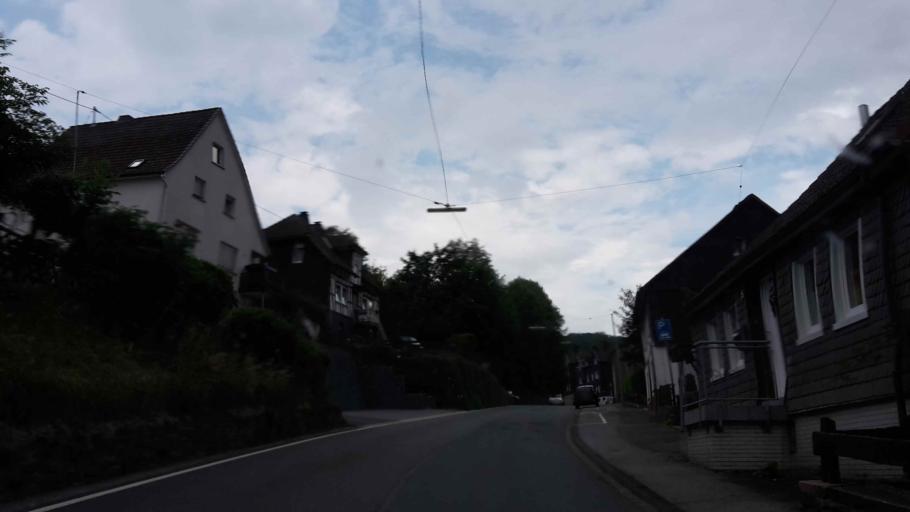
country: DE
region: North Rhine-Westphalia
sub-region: Regierungsbezirk Arnsberg
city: Lennestadt
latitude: 51.1256
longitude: 8.0695
